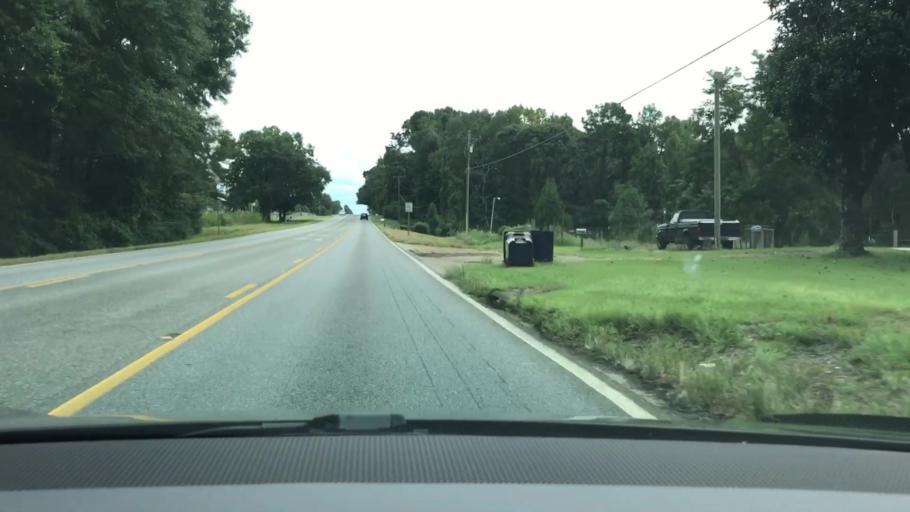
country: US
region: Alabama
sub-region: Pike County
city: Troy
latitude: 31.6862
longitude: -85.9596
